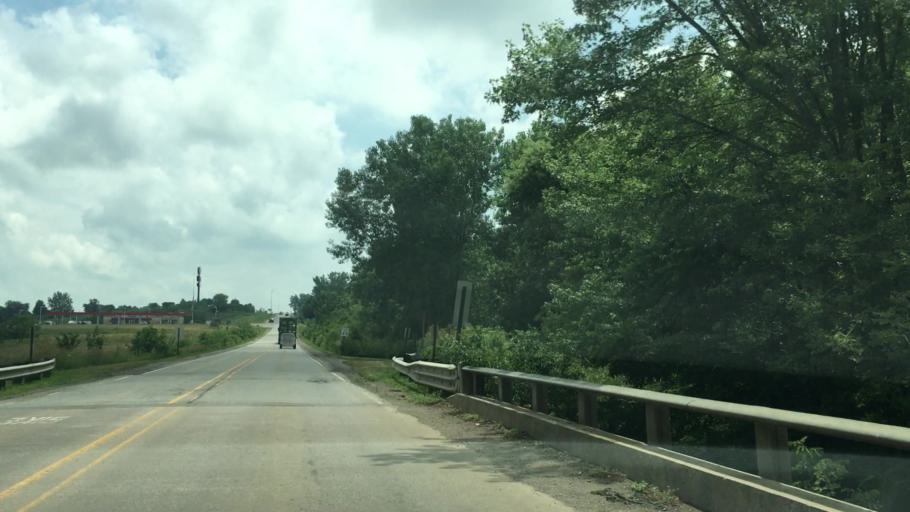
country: US
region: Iowa
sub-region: Johnson County
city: Tiffin
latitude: 41.7006
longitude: -91.6666
